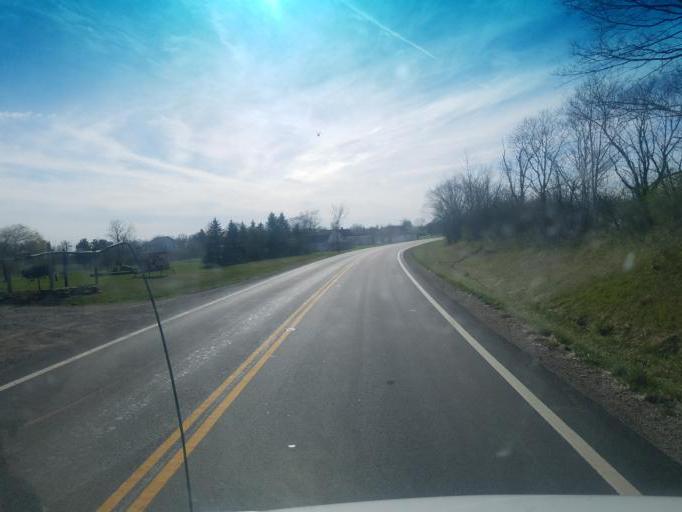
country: US
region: Ohio
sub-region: Union County
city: Marysville
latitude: 40.3312
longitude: -83.4588
